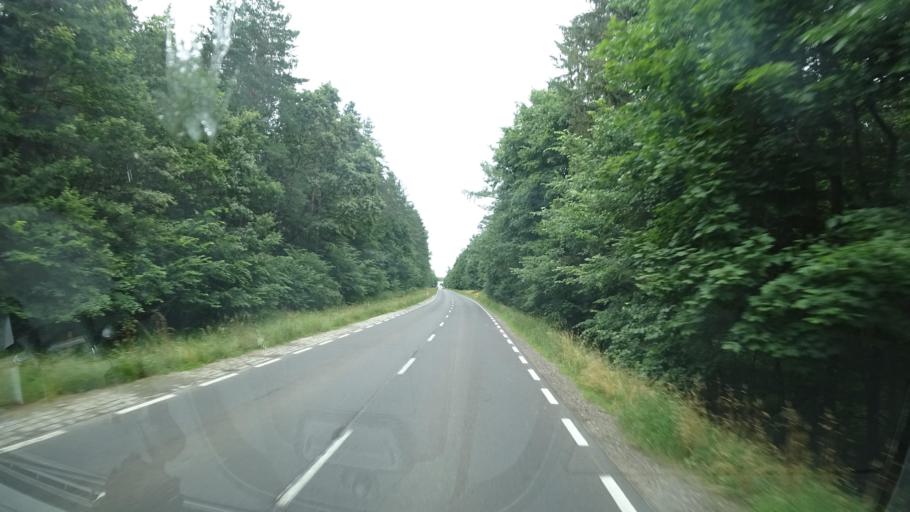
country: PL
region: Warmian-Masurian Voivodeship
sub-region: Powiat goldapski
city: Goldap
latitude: 54.3273
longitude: 22.2976
